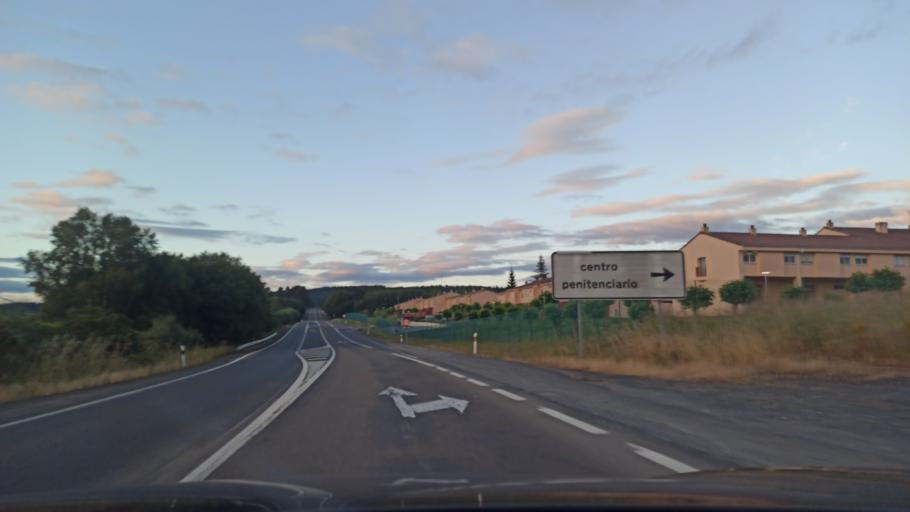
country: ES
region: Galicia
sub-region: Provincia de Lugo
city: Monterroso
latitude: 42.8095
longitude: -7.7736
